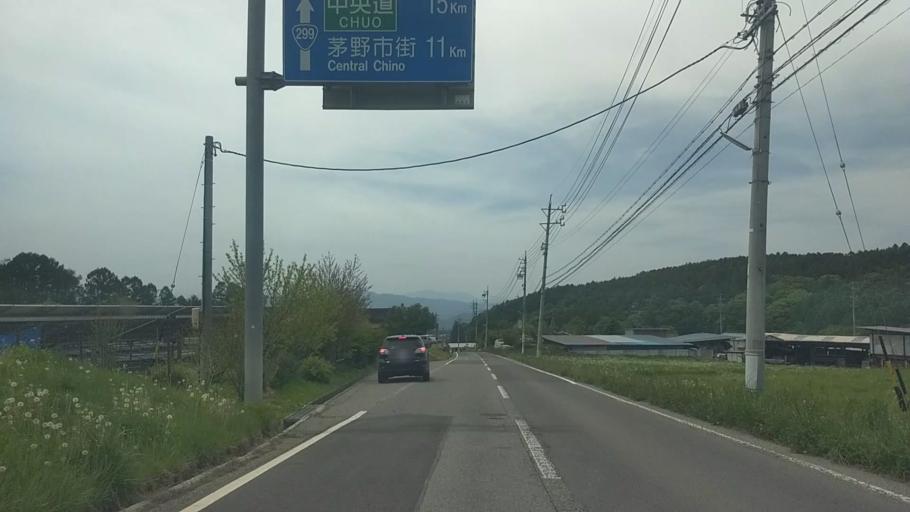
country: JP
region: Nagano
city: Chino
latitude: 36.0345
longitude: 138.2566
